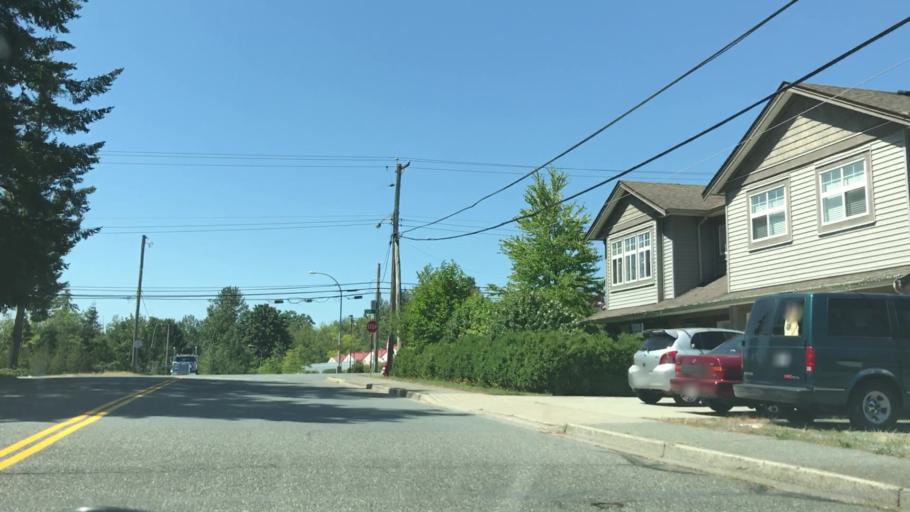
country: CA
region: British Columbia
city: Aldergrove
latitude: 49.0555
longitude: -122.4919
